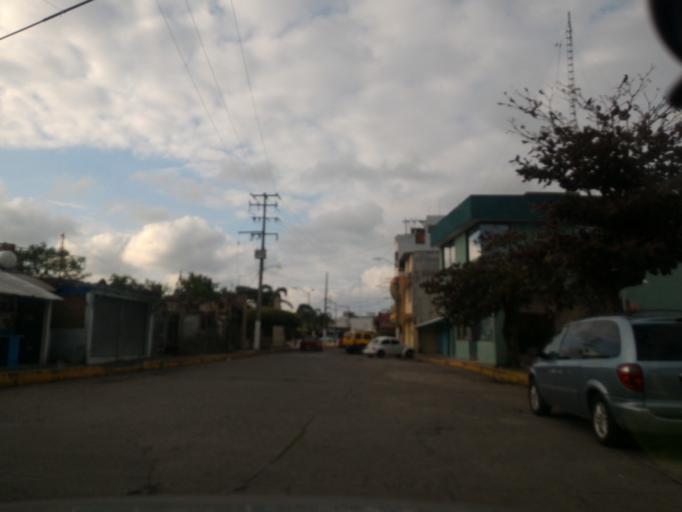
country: MX
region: Veracruz
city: San Rafael
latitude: 20.1884
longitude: -96.8653
